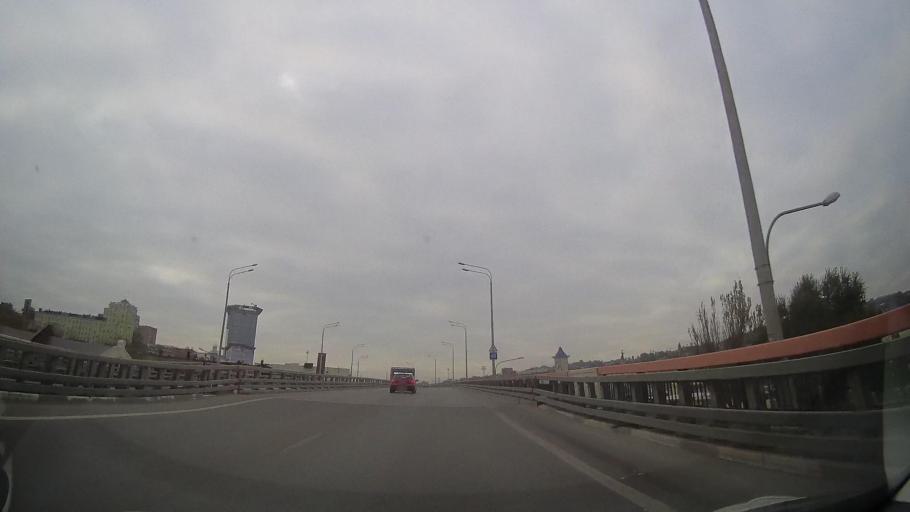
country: RU
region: Rostov
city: Rostov-na-Donu
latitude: 47.2198
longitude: 39.6950
